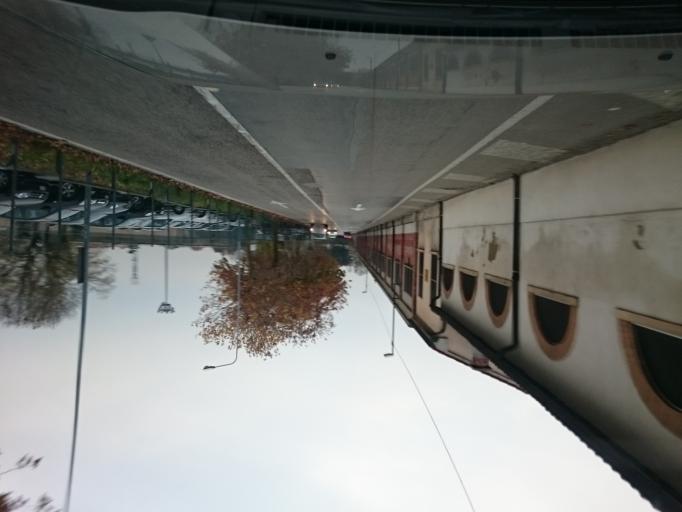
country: IT
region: Veneto
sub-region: Provincia di Padova
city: Padova
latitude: 45.3958
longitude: 11.8770
